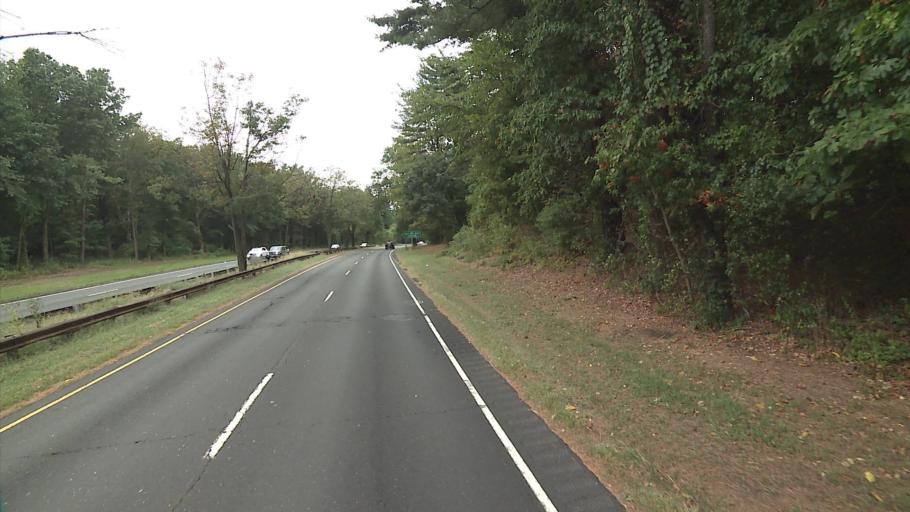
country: US
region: Connecticut
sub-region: Fairfield County
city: Norwalk
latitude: 41.1444
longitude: -73.4196
